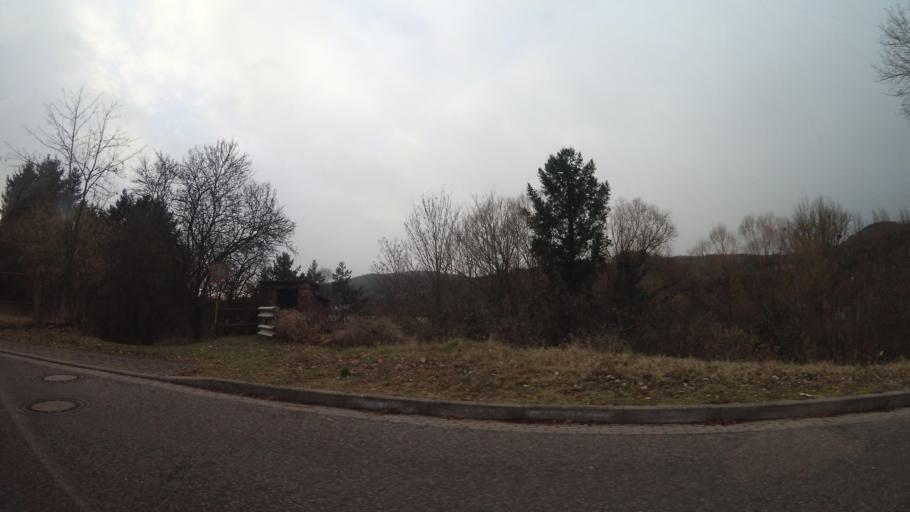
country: DE
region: Rheinland-Pfalz
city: Sankt Julian
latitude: 49.6097
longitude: 7.5299
